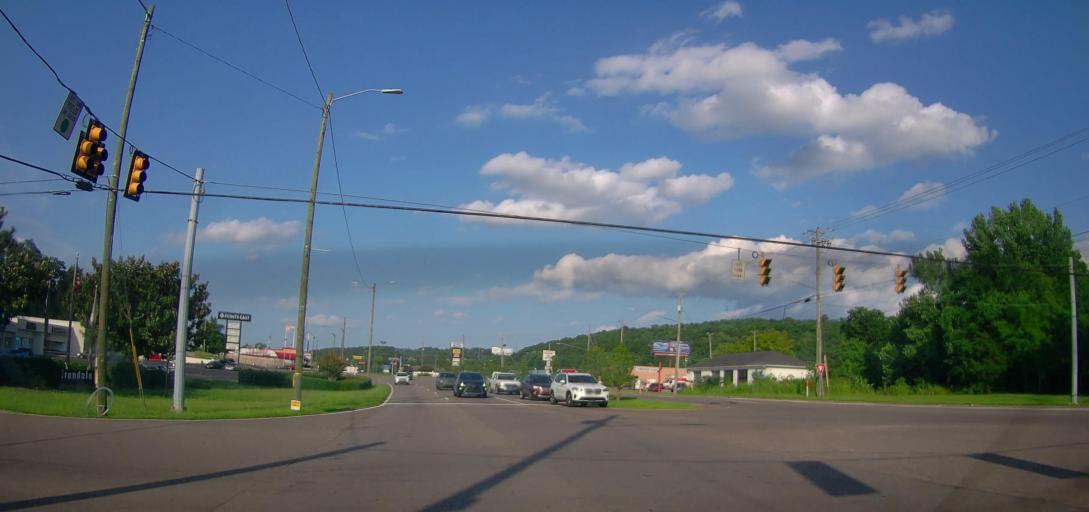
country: US
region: Alabama
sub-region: Jefferson County
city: Irondale
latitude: 33.5314
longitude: -86.7086
